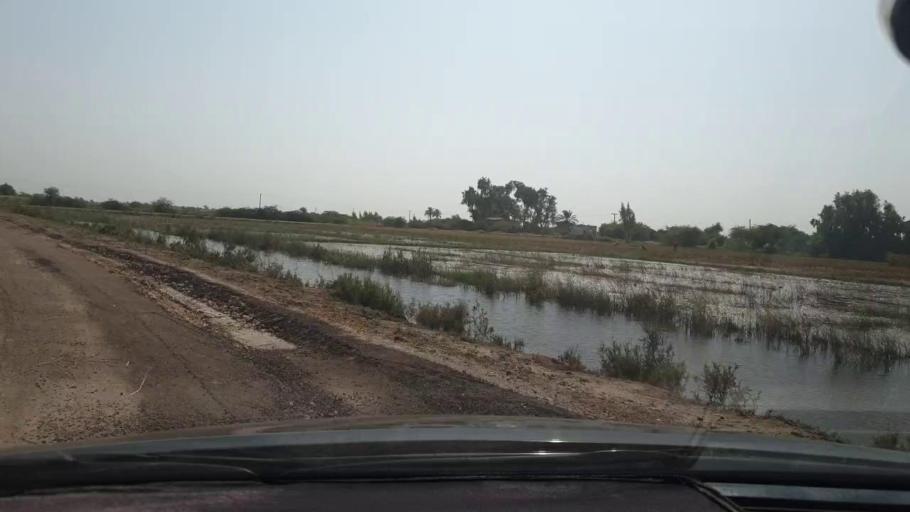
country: PK
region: Sindh
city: Tando Bago
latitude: 24.6987
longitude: 69.1063
